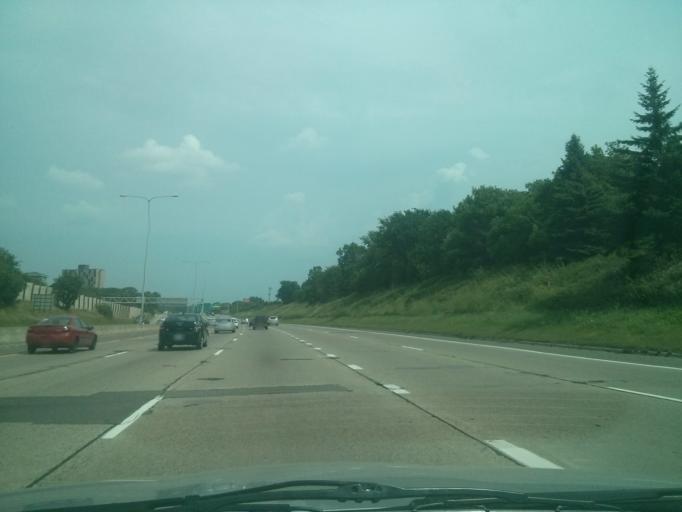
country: US
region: Minnesota
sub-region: Ramsey County
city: Saint Paul
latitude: 44.9517
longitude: -93.0551
